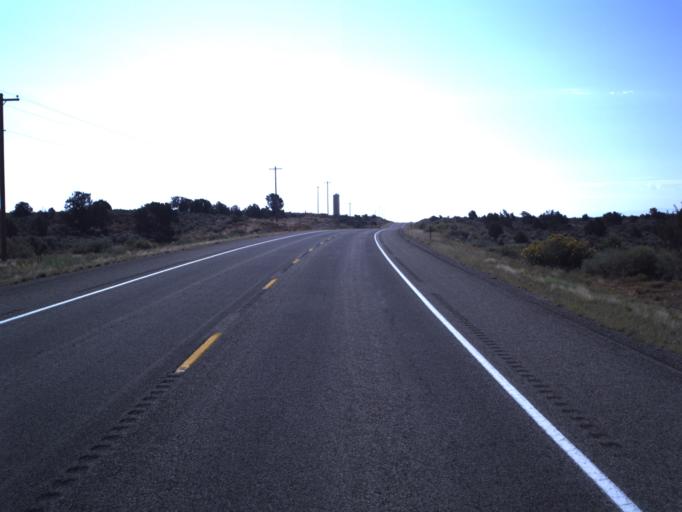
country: US
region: Utah
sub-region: San Juan County
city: Blanding
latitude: 37.4876
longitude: -109.4763
